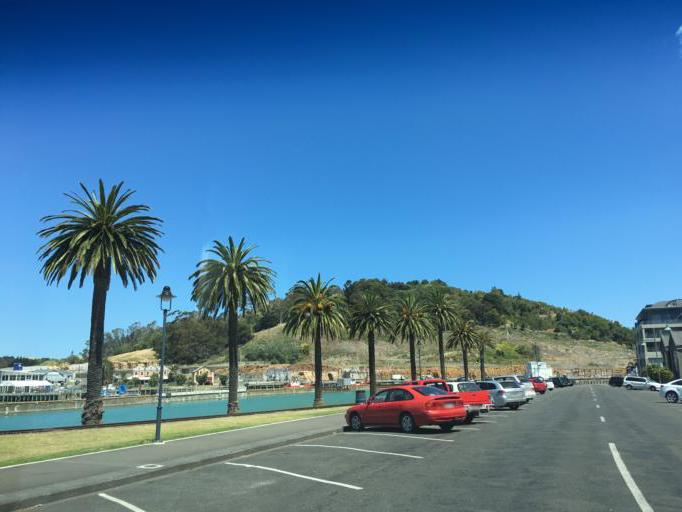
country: NZ
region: Gisborne
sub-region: Gisborne District
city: Gisborne
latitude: -38.6697
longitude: 178.0276
